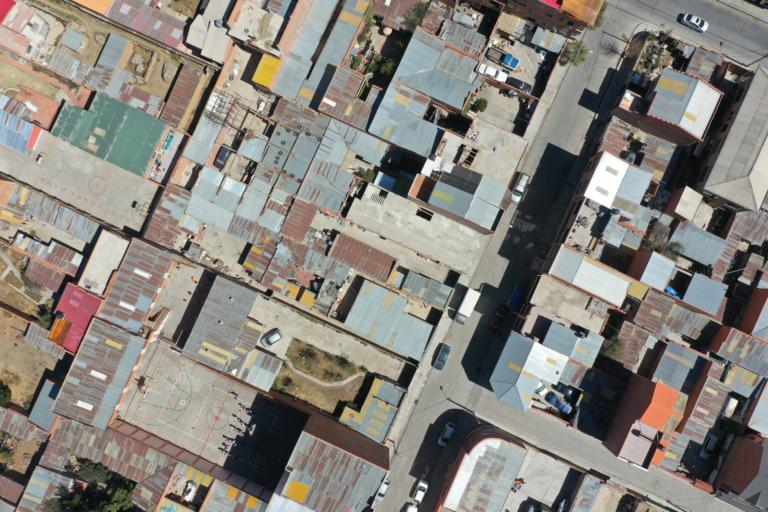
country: BO
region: La Paz
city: La Paz
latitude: -16.5343
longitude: -68.1510
